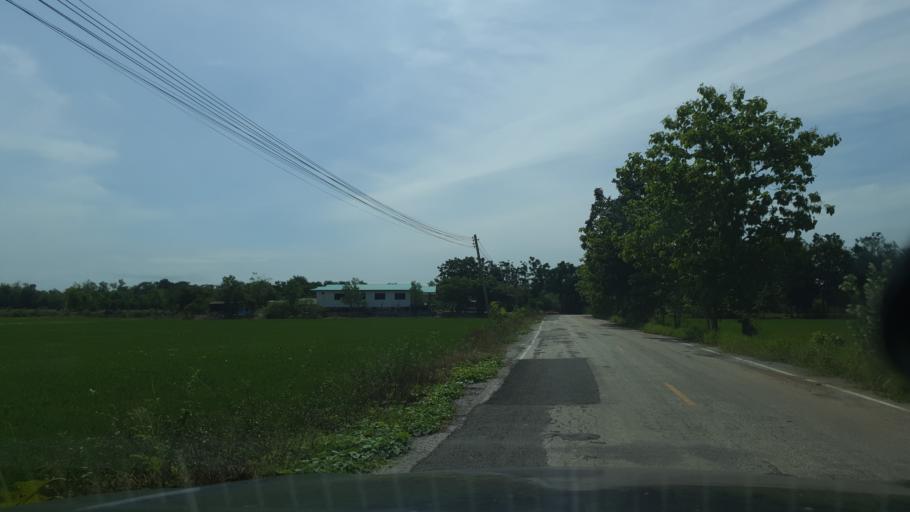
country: TH
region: Sukhothai
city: Si Samrong
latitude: 17.1957
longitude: 99.7312
